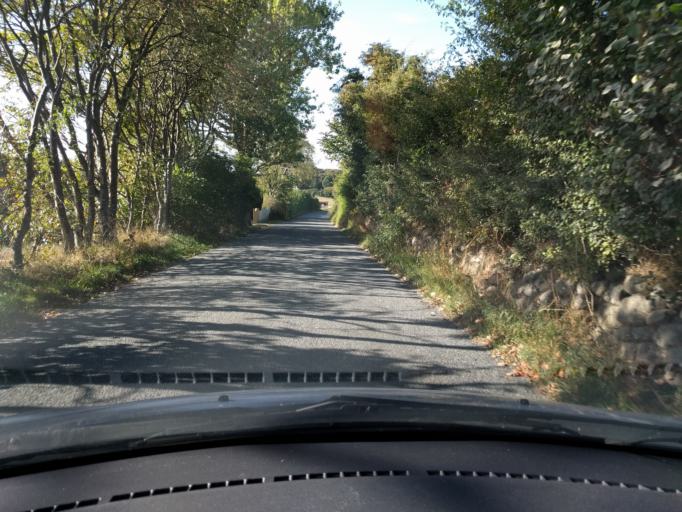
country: DK
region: South Denmark
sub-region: Assens Kommune
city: Harby
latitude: 55.1331
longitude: 10.0298
